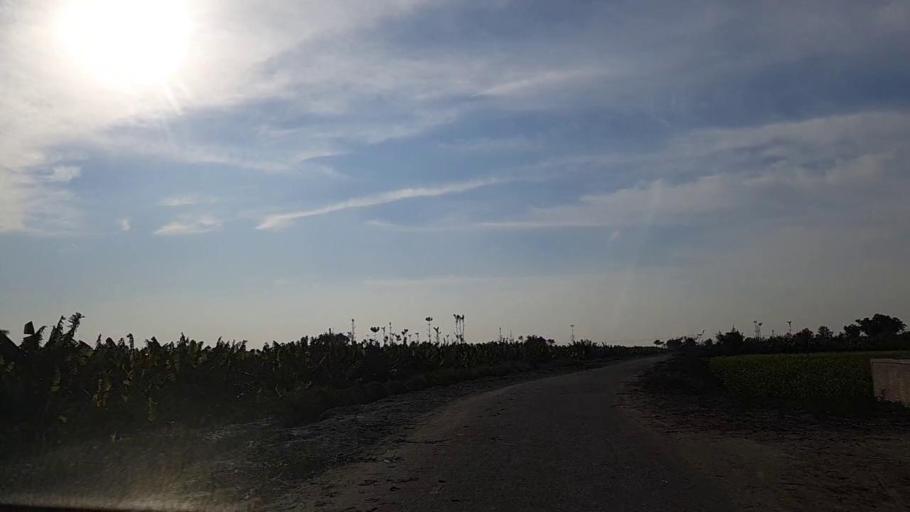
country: PK
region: Sindh
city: Bandhi
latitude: 26.5803
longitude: 68.2933
